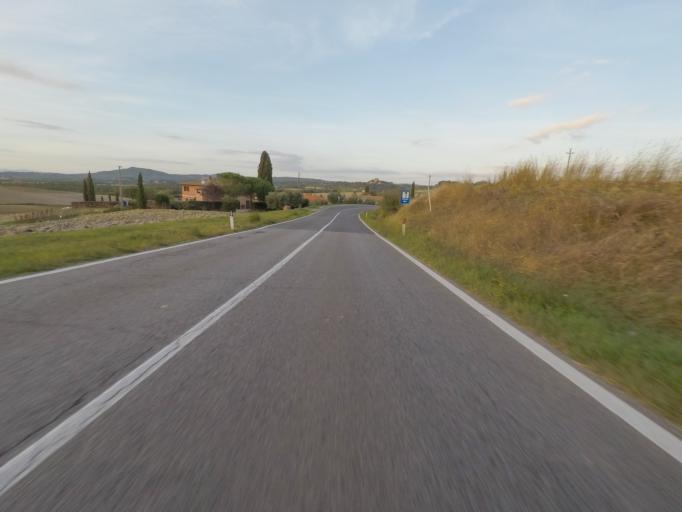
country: IT
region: Tuscany
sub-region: Provincia di Siena
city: Pienza
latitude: 43.0910
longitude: 11.6864
